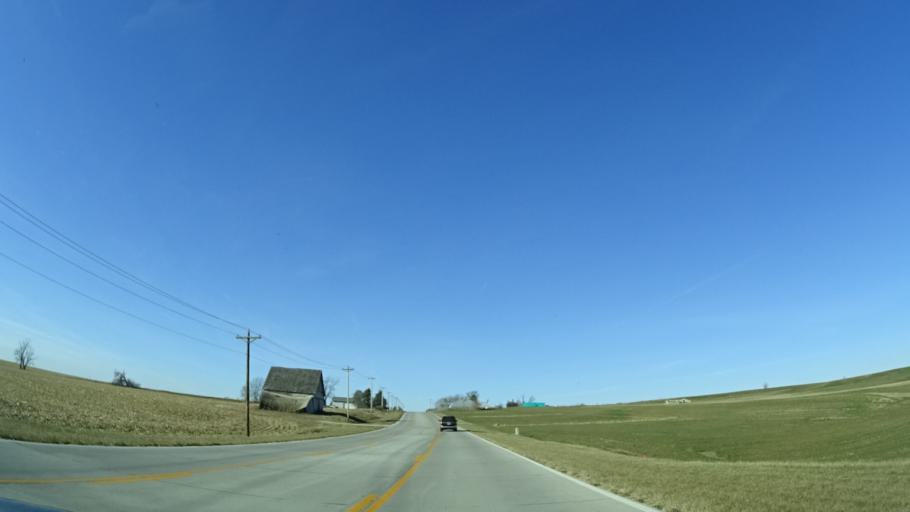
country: US
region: Nebraska
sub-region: Sarpy County
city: Papillion
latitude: 41.1179
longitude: -96.0296
